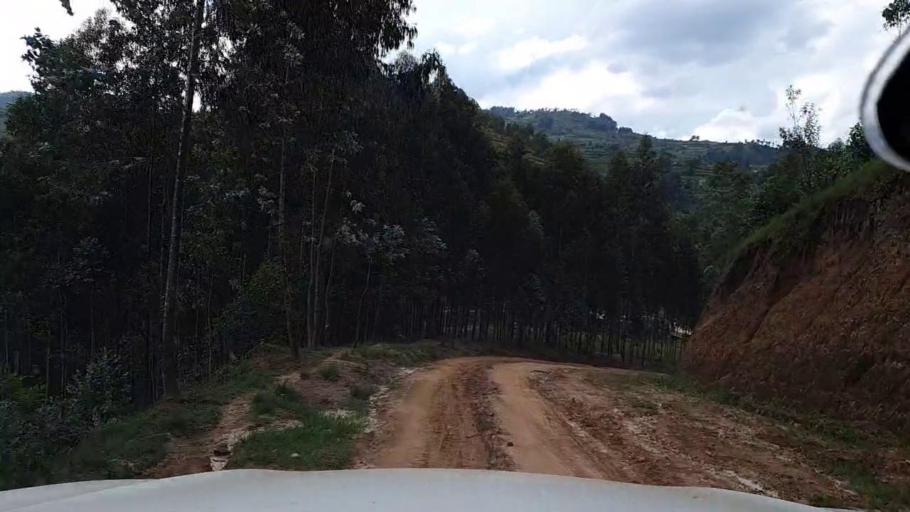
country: RW
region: Southern Province
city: Nzega
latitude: -2.6986
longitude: 29.4389
